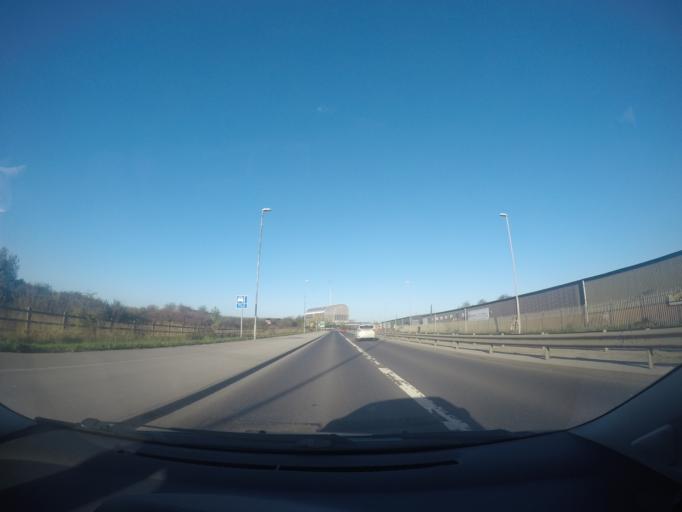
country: GB
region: England
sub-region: City and Borough of Leeds
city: Leeds
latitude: 53.7852
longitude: -1.4962
